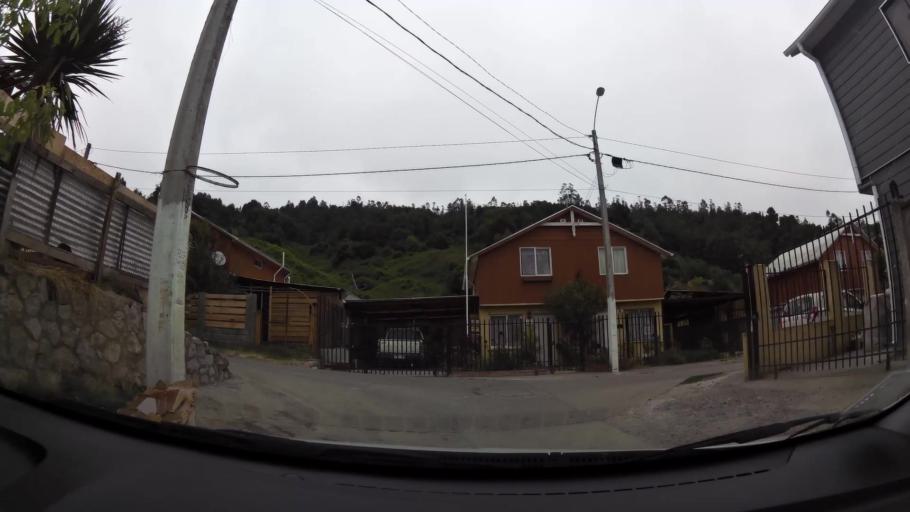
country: CL
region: Biobio
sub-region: Provincia de Concepcion
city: Concepcion
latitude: -36.8345
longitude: -73.0113
